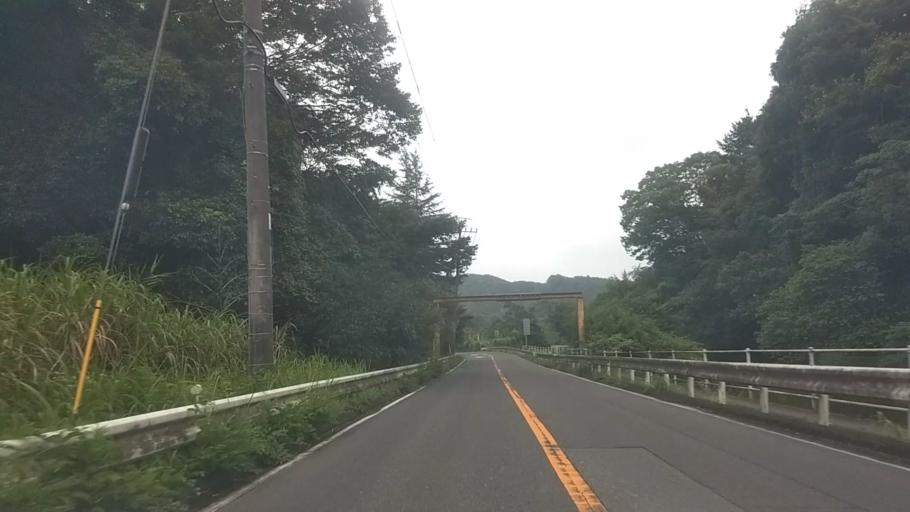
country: JP
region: Chiba
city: Kawaguchi
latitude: 35.2516
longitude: 140.0721
